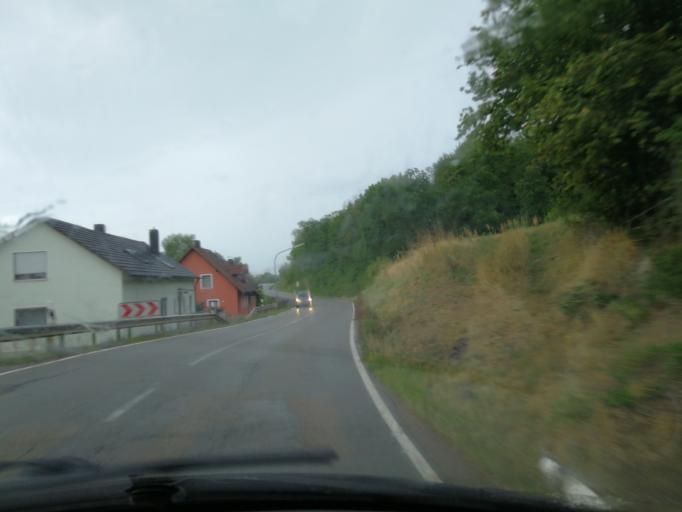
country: DE
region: Bavaria
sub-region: Upper Palatinate
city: Donaustauf
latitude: 49.0243
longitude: 12.2588
